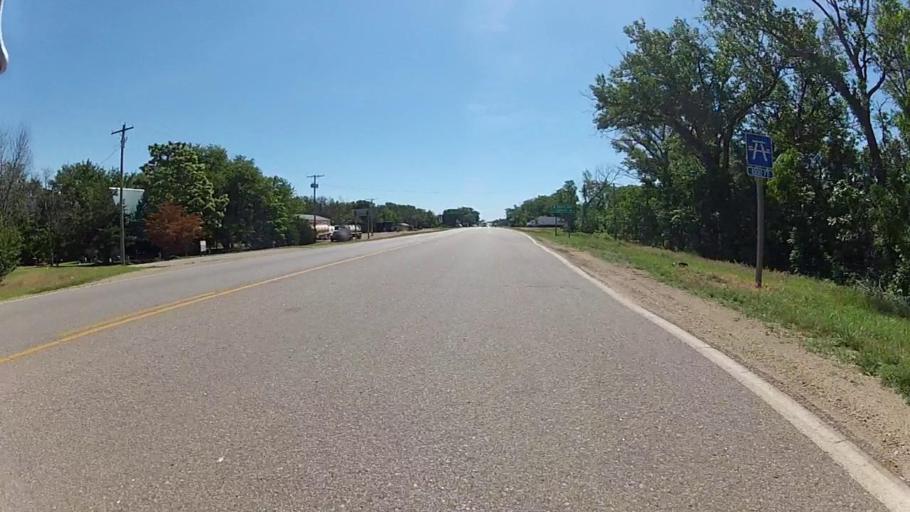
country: US
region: Kansas
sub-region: Barber County
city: Medicine Lodge
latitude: 37.2753
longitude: -98.6000
